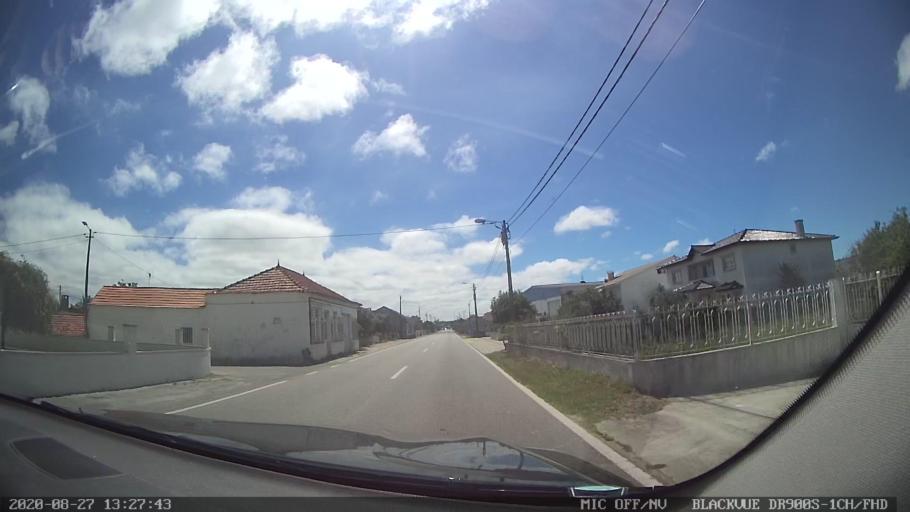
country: PT
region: Aveiro
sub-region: Vagos
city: Vagos
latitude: 40.5279
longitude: -8.6791
